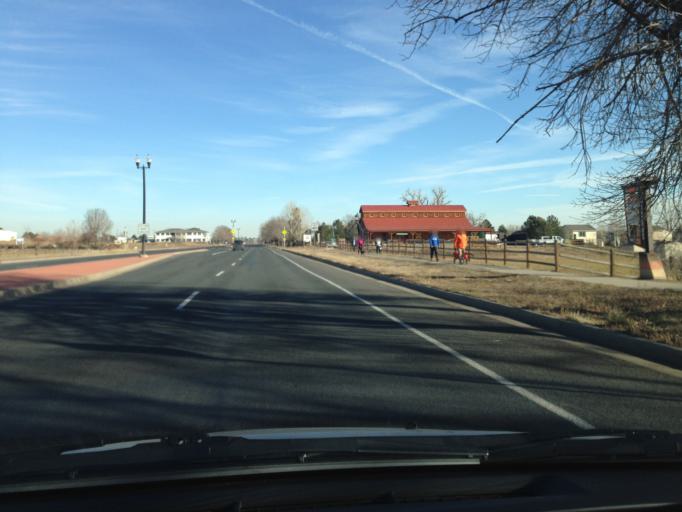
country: US
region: Colorado
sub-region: Boulder County
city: Lafayette
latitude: 40.0001
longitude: -105.1116
